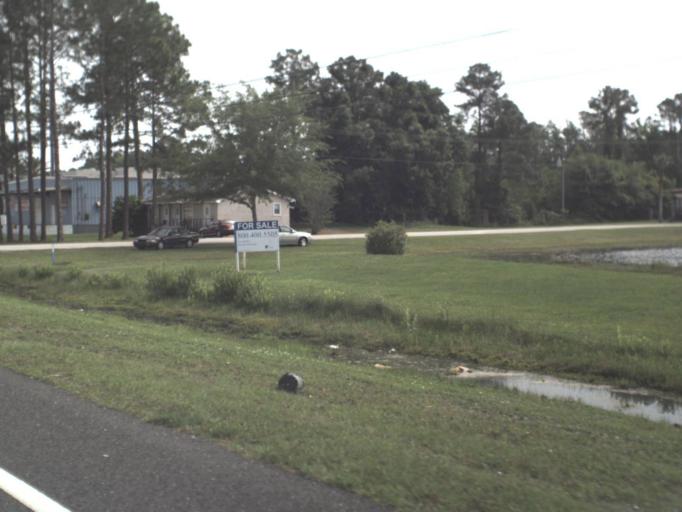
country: US
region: Florida
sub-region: Clay County
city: Orange Park
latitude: 30.1170
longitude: -81.7047
